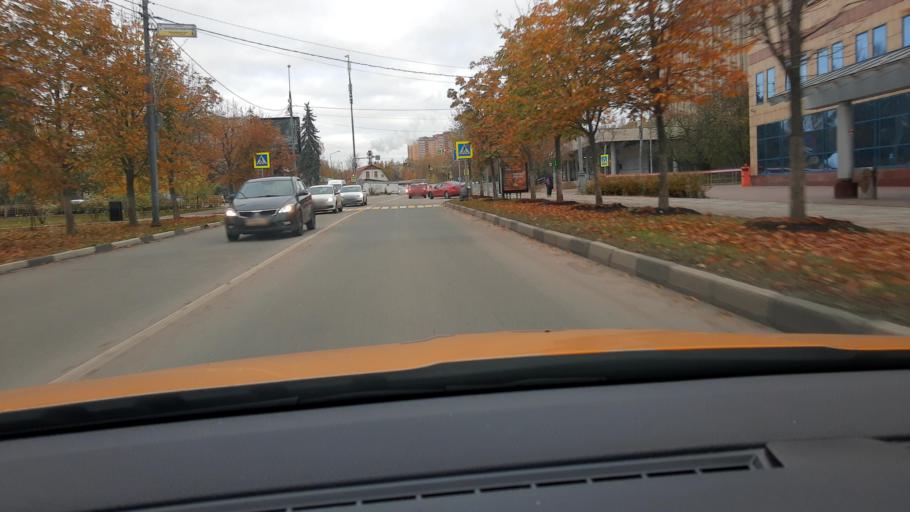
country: RU
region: Moskovskaya
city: Odintsovo
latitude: 55.6789
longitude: 37.2667
